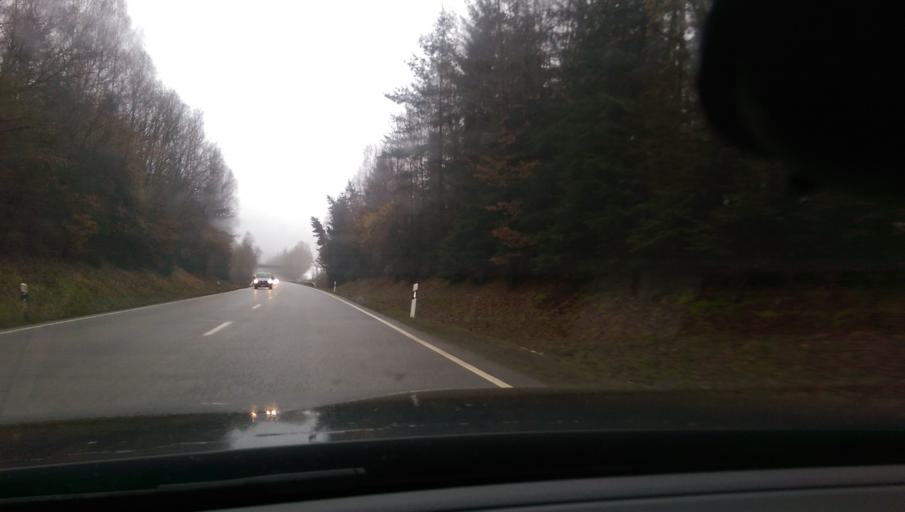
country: DE
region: Bavaria
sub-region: Lower Bavaria
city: Tiefenbach
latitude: 48.6007
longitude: 13.4107
